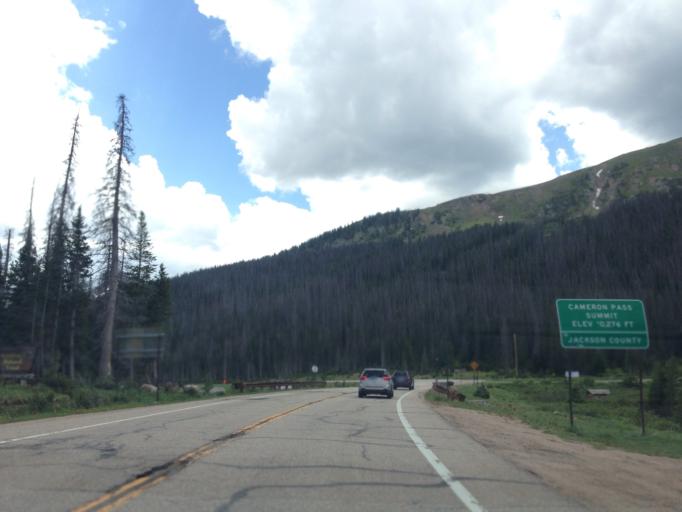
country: US
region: Colorado
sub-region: Larimer County
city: Estes Park
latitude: 40.5211
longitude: -105.8920
